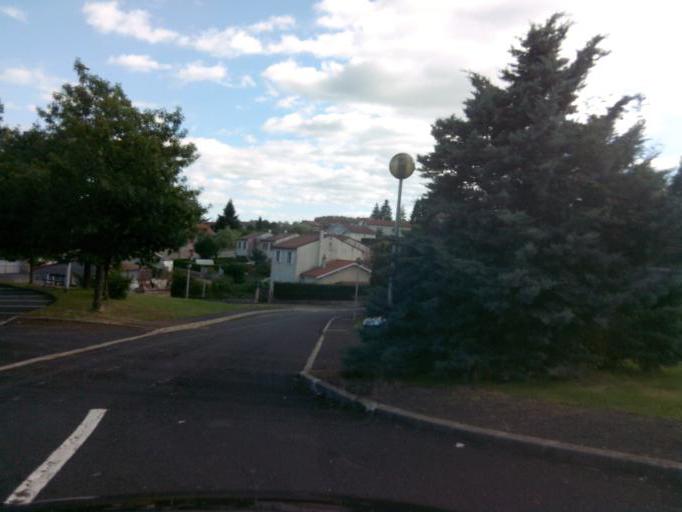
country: FR
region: Auvergne
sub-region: Departement de la Haute-Loire
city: Craponne-sur-Arzon
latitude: 45.3302
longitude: 3.8438
